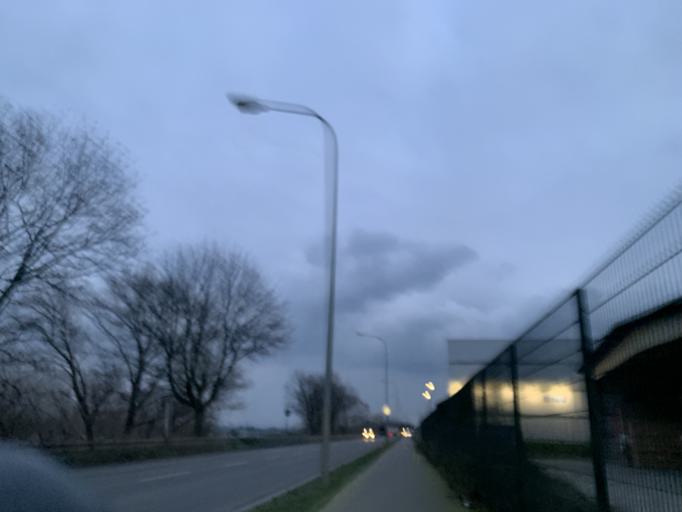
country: DE
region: North Rhine-Westphalia
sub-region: Regierungsbezirk Dusseldorf
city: Meerbusch
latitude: 51.3431
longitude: 6.6734
